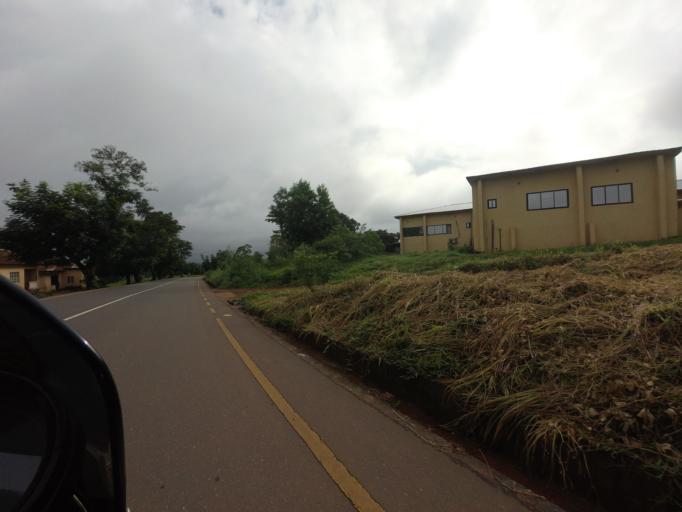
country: SL
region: Northern Province
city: Kambia
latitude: 9.1171
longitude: -12.9233
